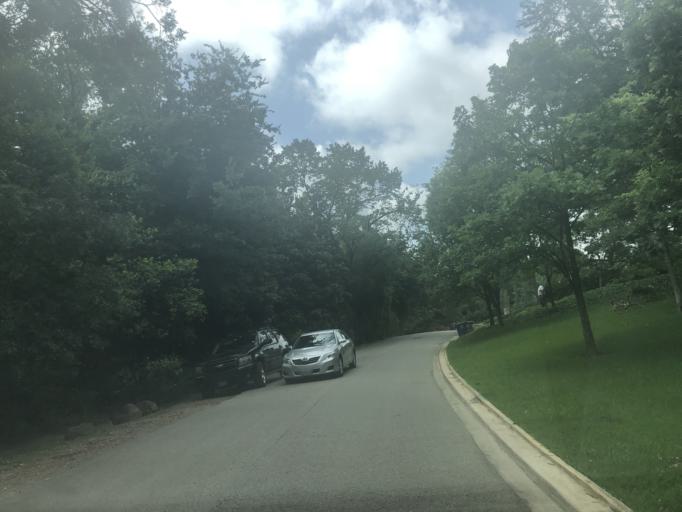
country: US
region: Texas
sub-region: Dallas County
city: University Park
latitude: 32.8616
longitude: -96.8292
